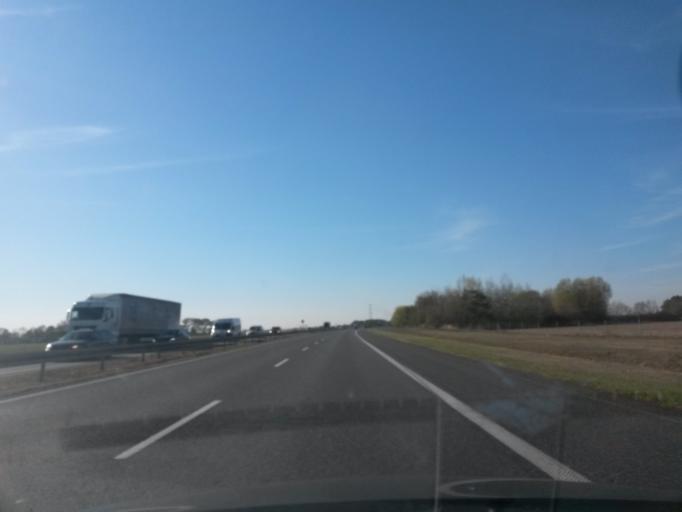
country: PL
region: Opole Voivodeship
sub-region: Powiat brzeski
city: Grodkow
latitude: 50.7697
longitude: 17.3900
